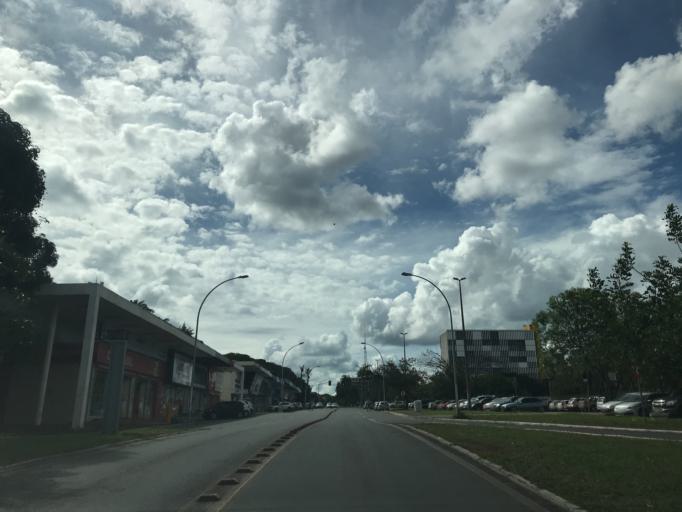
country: BR
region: Federal District
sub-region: Brasilia
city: Brasilia
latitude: -15.8027
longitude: -47.8881
